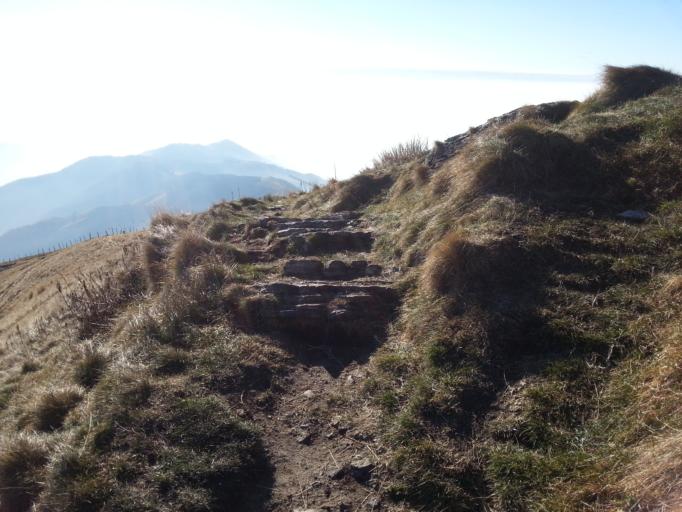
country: CH
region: Ticino
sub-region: Lugano District
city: Melano
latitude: 45.9306
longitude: 9.0199
